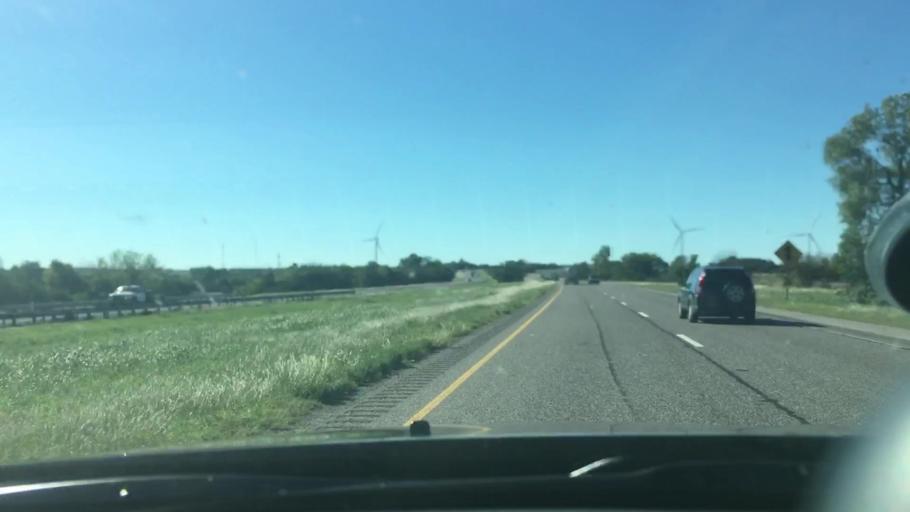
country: US
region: Oklahoma
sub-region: Murray County
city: Davis
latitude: 34.3988
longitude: -97.1417
